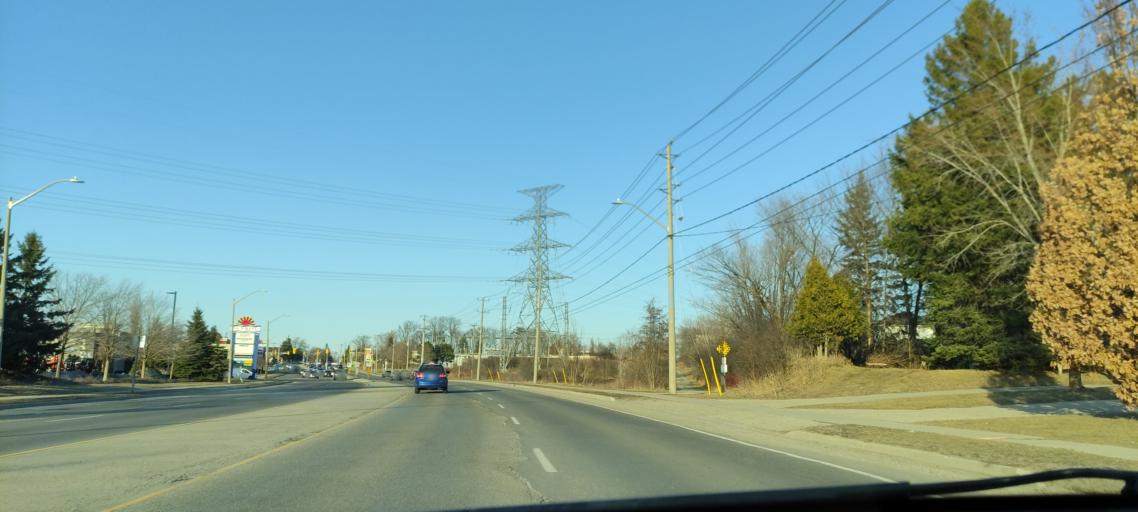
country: CA
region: Ontario
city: Kitchener
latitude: 43.4133
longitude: -80.5154
